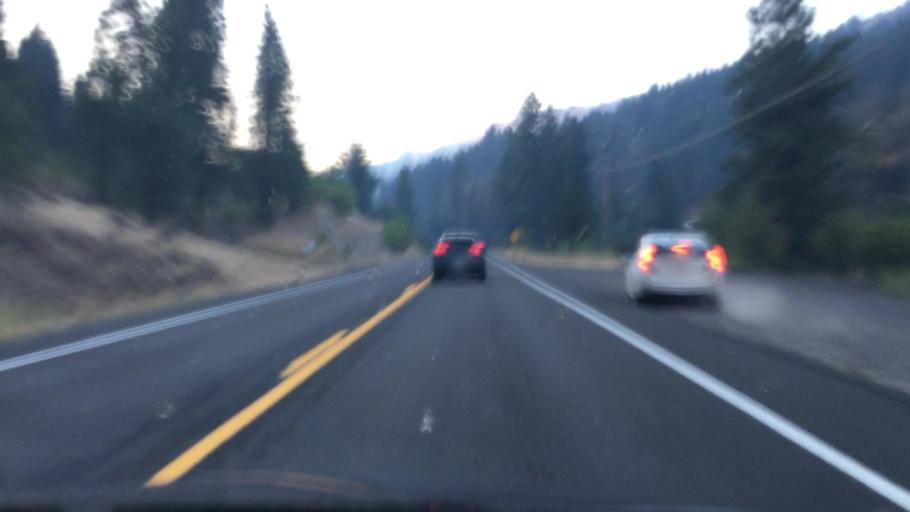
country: US
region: Idaho
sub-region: Valley County
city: McCall
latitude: 45.2083
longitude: -116.3131
